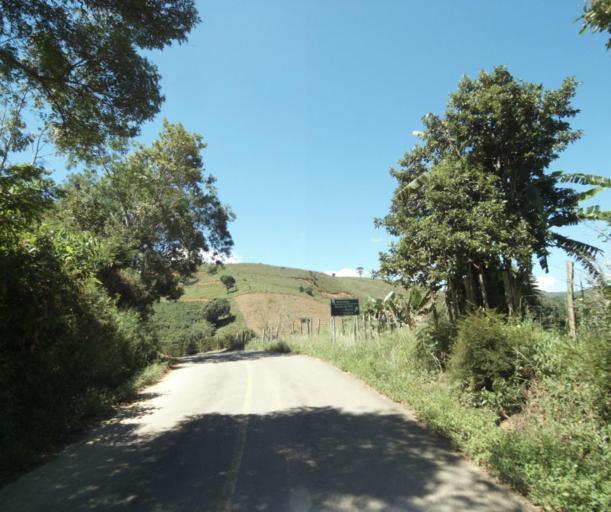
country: BR
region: Minas Gerais
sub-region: Espera Feliz
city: Espera Feliz
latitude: -20.6408
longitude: -41.8082
